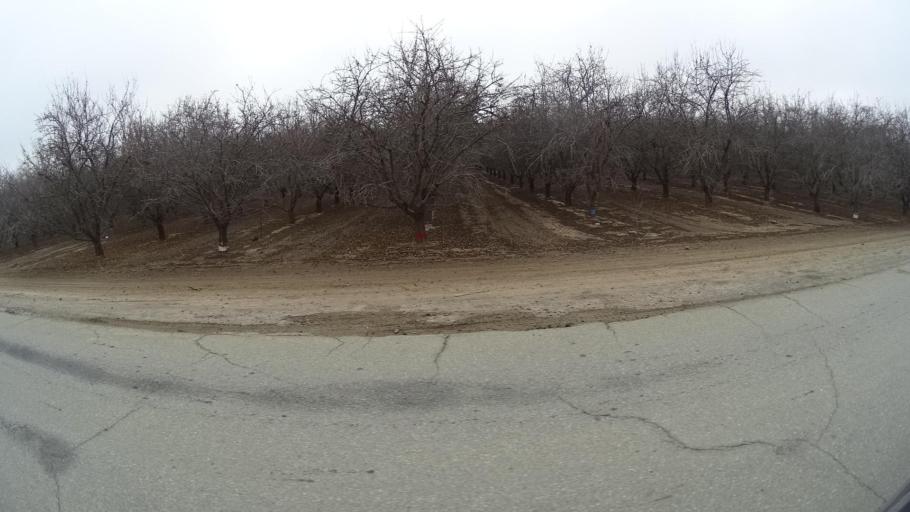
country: US
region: California
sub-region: Kern County
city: Maricopa
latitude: 35.0938
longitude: -119.2854
